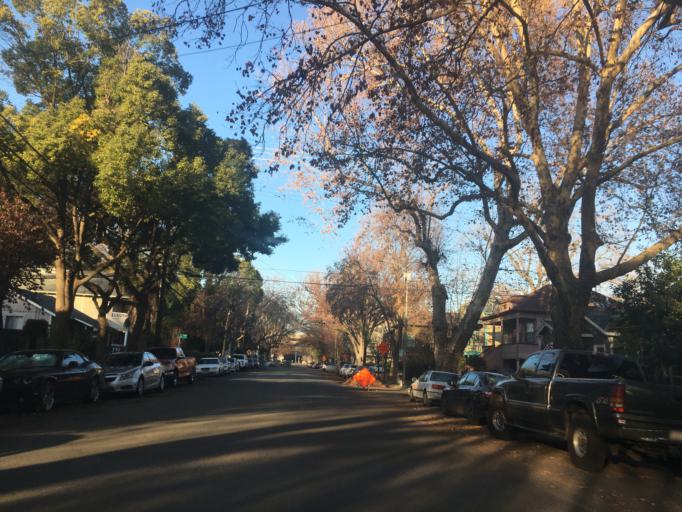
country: US
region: California
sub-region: Sacramento County
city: Sacramento
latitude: 38.5704
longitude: -121.5066
